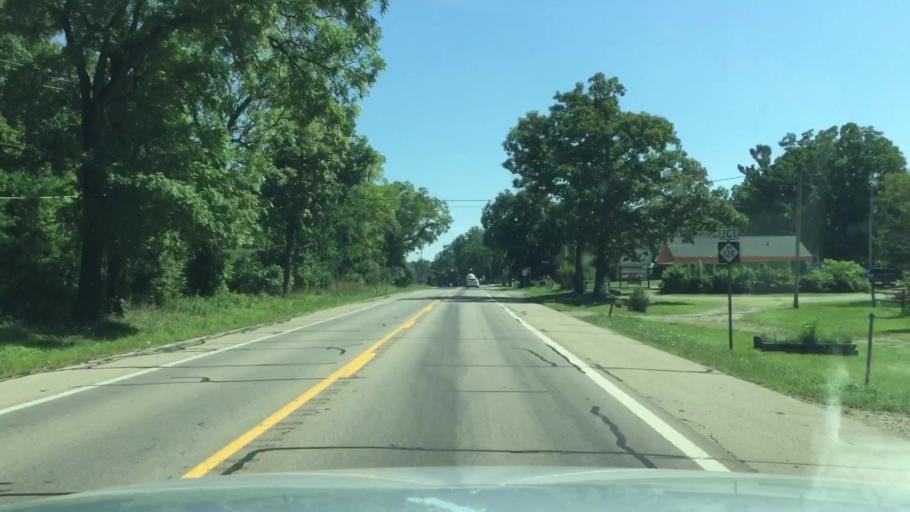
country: US
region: Michigan
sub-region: Jackson County
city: Brooklyn
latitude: 42.0567
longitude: -84.1442
